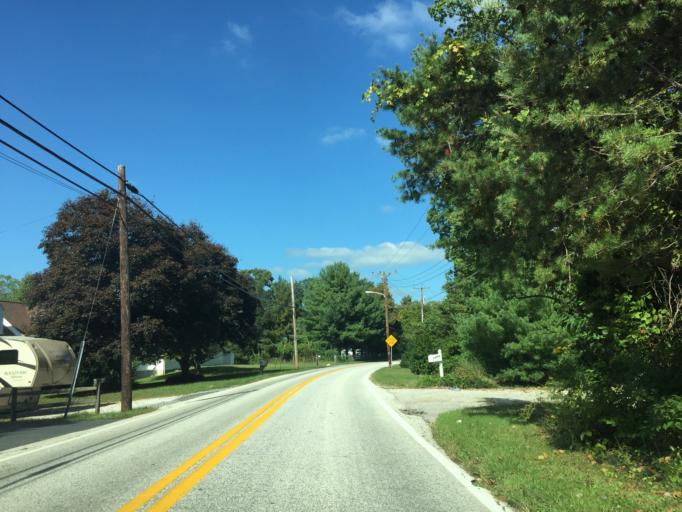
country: US
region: Maryland
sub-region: Baltimore County
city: Carney
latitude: 39.4057
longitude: -76.5435
